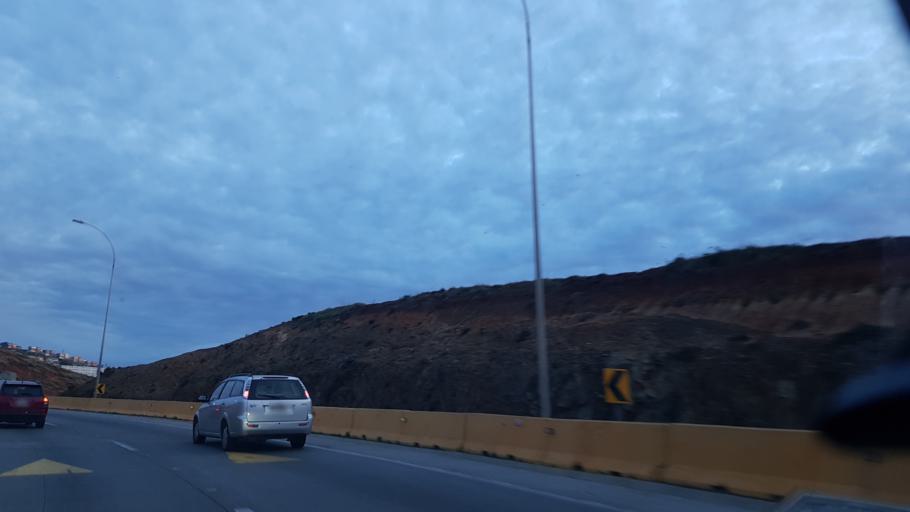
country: CL
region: Valparaiso
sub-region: Provincia de Valparaiso
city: Valparaiso
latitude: -33.0326
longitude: -71.6559
